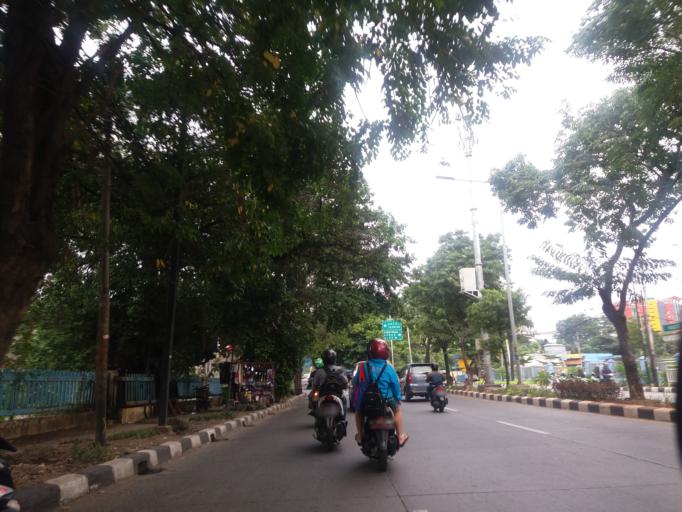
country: ID
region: Jakarta Raya
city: Jakarta
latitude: -6.1452
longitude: 106.8331
